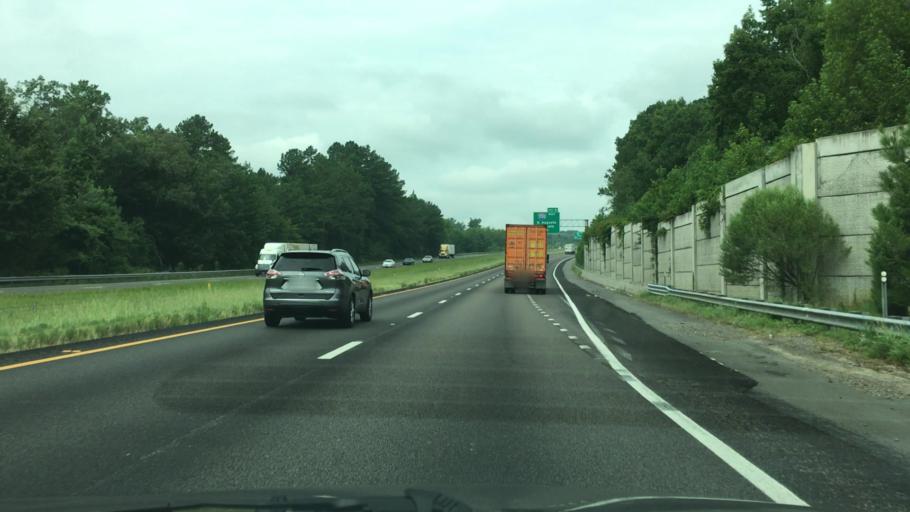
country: US
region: South Carolina
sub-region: Edgefield County
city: Murphys Estates
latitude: 33.5712
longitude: -81.9141
